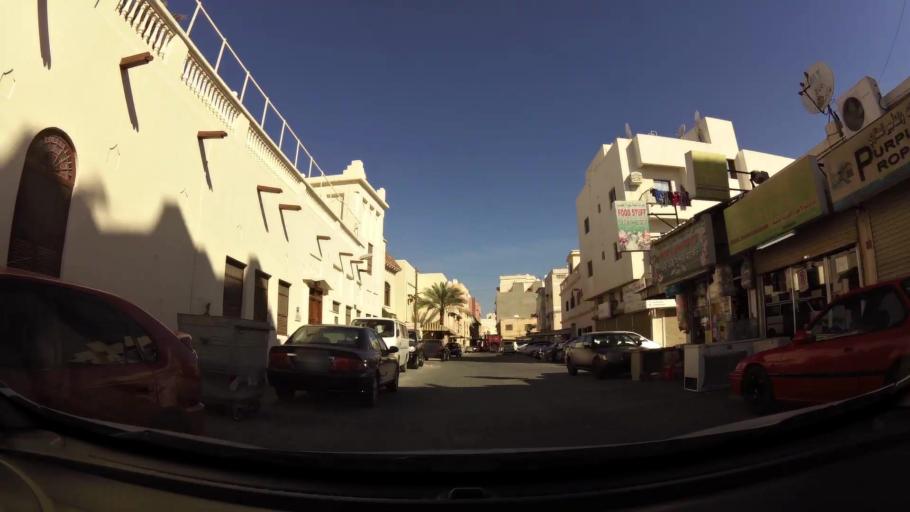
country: BH
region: Muharraq
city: Al Muharraq
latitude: 26.2595
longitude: 50.6128
